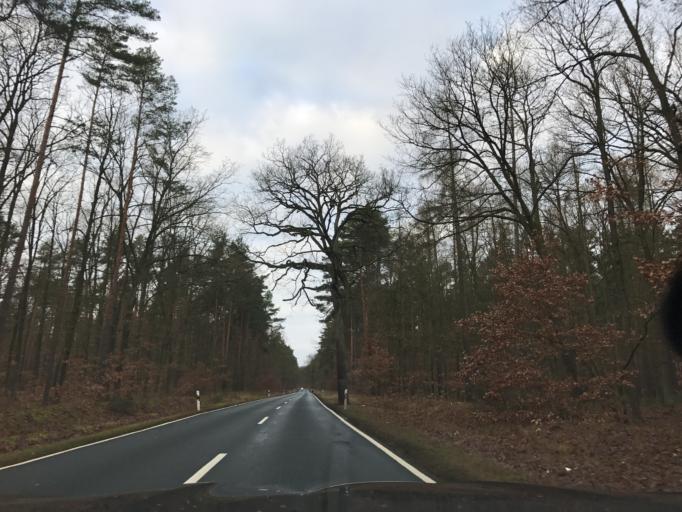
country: DE
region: Brandenburg
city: Gross Kreutz
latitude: 52.3317
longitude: 12.7235
